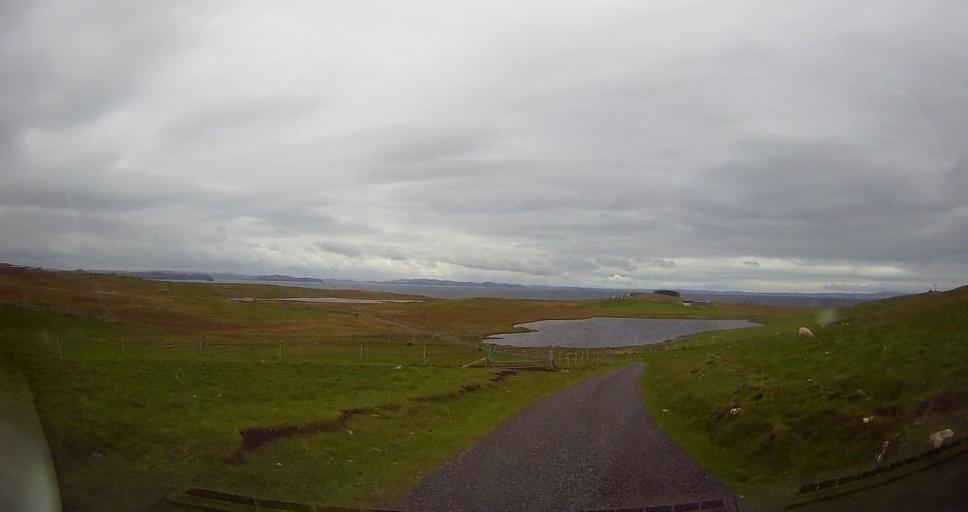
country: GB
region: Scotland
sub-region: Shetland Islands
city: Lerwick
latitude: 60.4876
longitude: -1.6153
